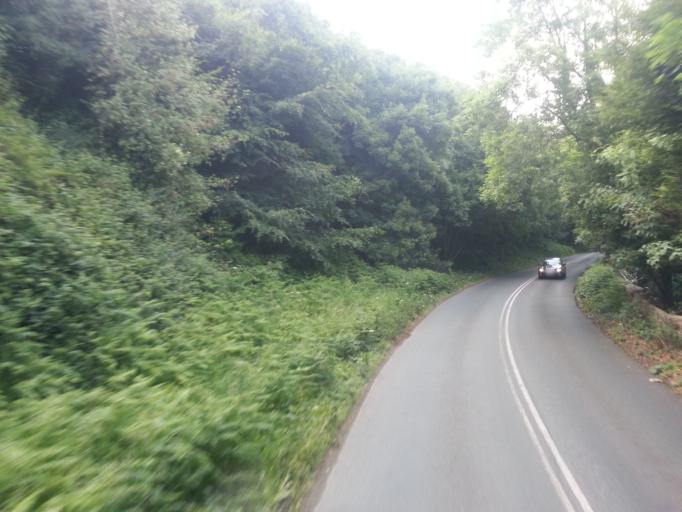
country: IE
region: Leinster
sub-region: Wicklow
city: Enniskerry
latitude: 53.2156
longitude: -6.1787
